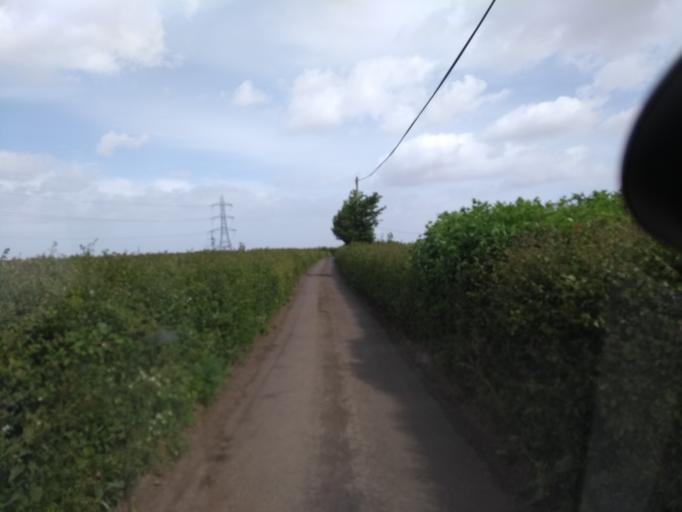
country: GB
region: England
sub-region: Somerset
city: Bridgwater
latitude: 51.1802
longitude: -3.0943
